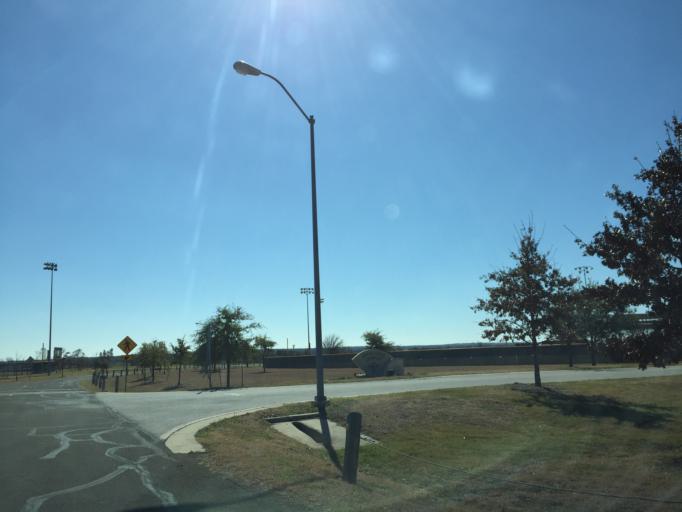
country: US
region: Texas
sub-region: Williamson County
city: Hutto
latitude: 30.5451
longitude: -97.6178
